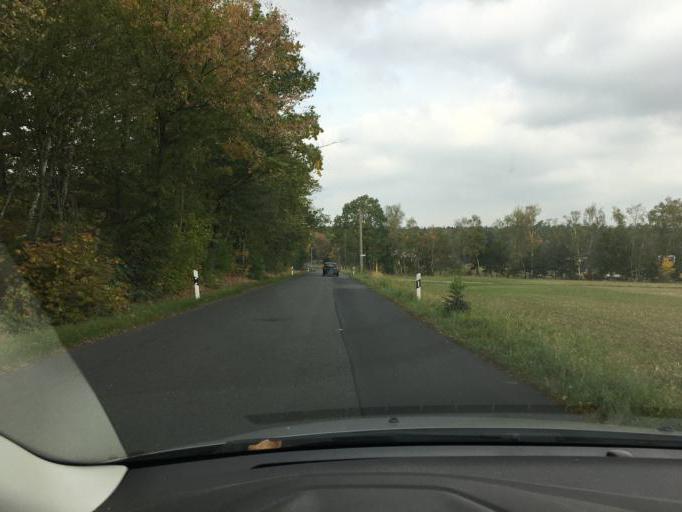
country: DE
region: Saxony
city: Freital
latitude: 50.9924
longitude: 13.6794
